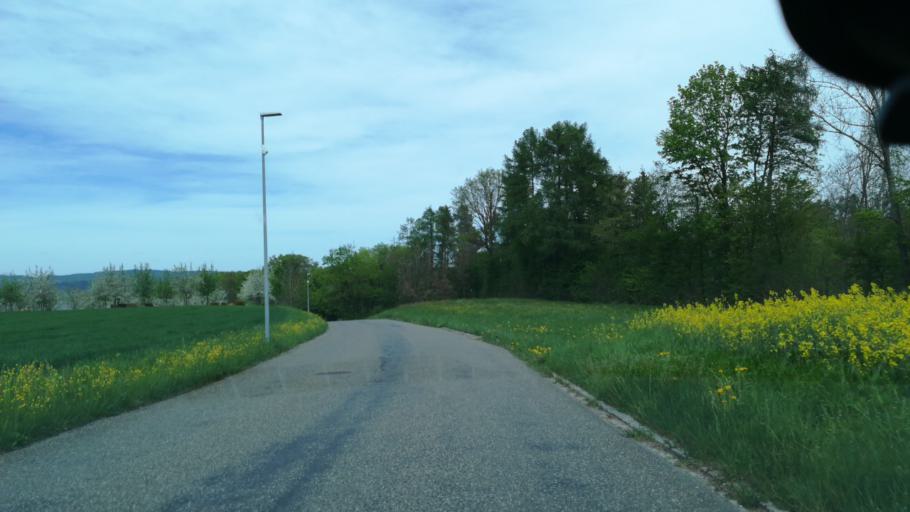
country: CH
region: Thurgau
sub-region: Kreuzlingen District
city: Ermatingen
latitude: 47.6624
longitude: 9.0804
